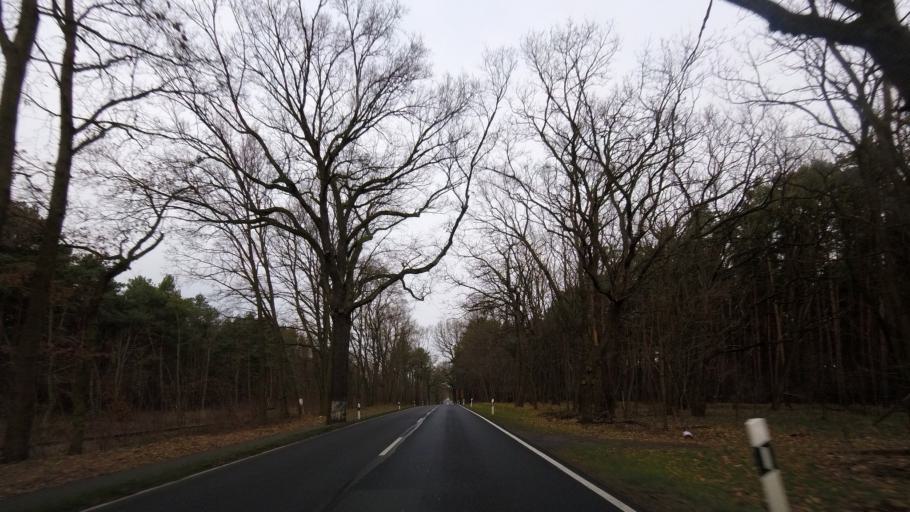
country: DE
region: Brandenburg
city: Treuenbrietzen
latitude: 52.0764
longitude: 12.8845
